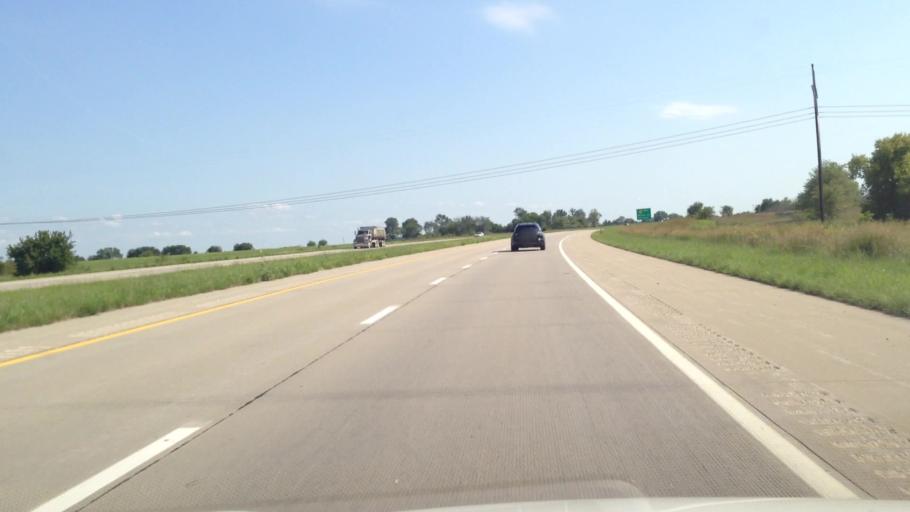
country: US
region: Kansas
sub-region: Linn County
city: Pleasanton
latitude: 38.2773
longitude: -94.6698
